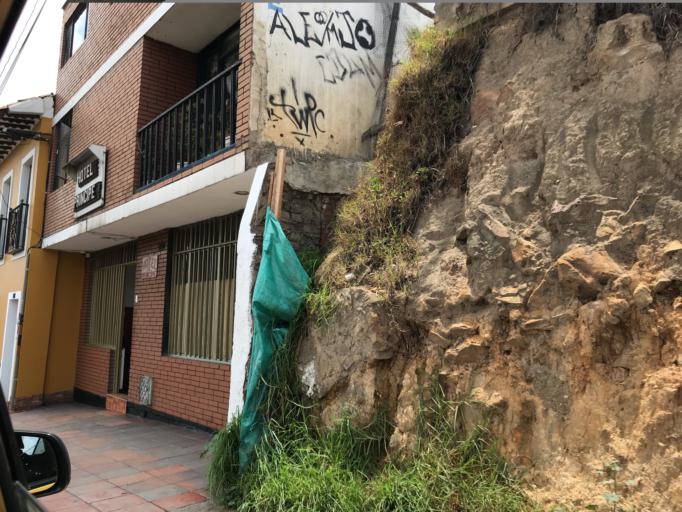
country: CO
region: Boyaca
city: Tunja
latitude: 5.5287
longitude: -73.3599
